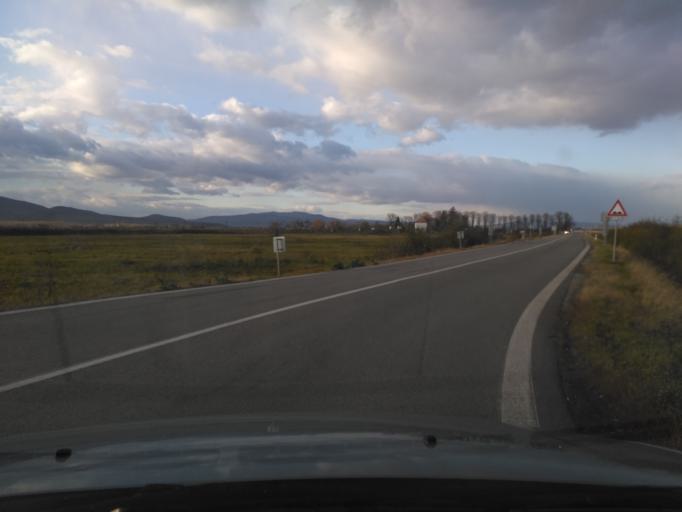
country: HU
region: Borsod-Abauj-Zemplen
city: Satoraljaujhely
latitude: 48.4117
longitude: 21.6660
